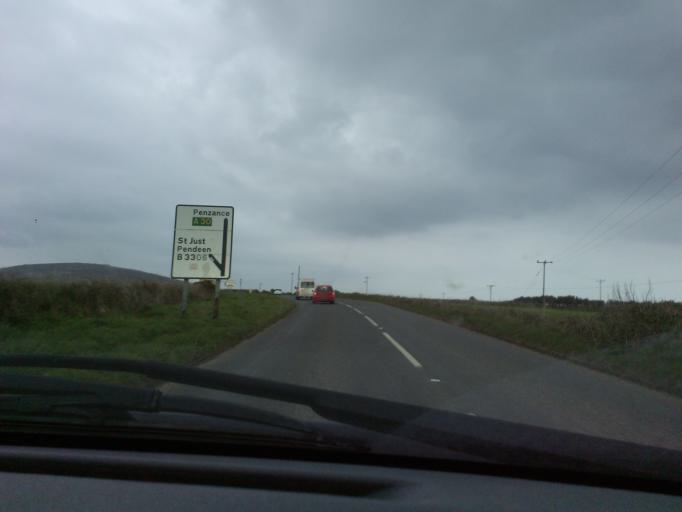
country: GB
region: England
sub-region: Cornwall
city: Sennen
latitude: 50.0871
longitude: -5.6718
